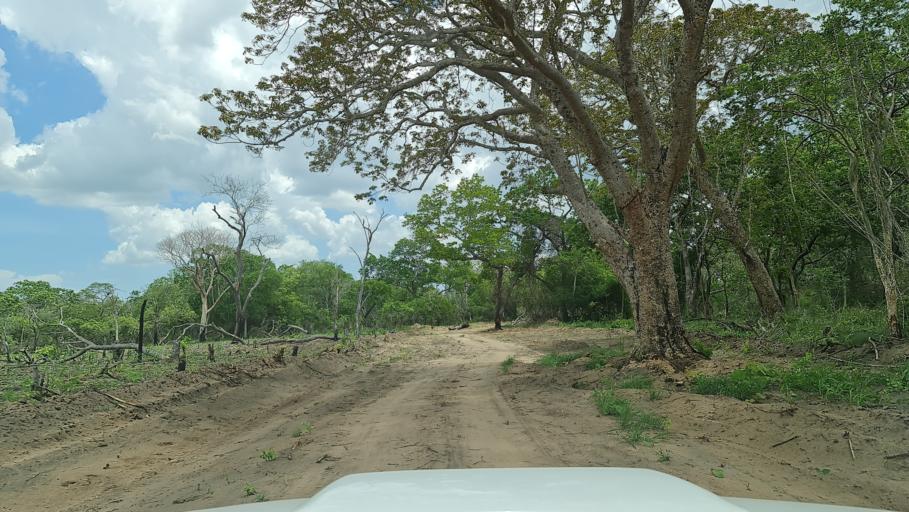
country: MZ
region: Nampula
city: Ilha de Mocambique
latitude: -15.2480
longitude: 40.3696
